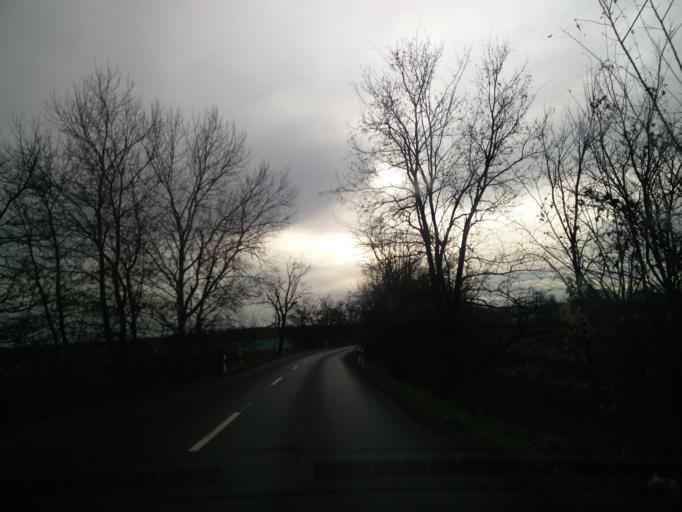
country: HU
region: Pest
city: Mogyorod
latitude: 47.6422
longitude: 19.2321
